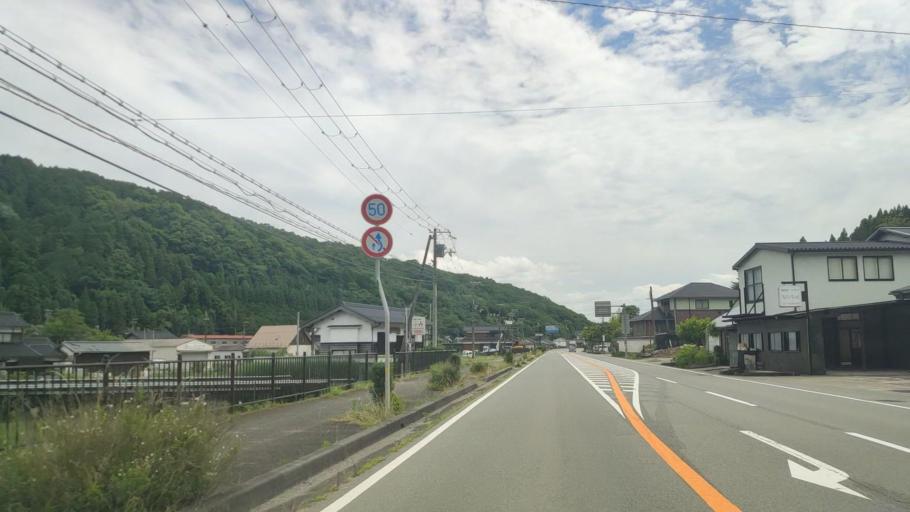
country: JP
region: Hyogo
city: Yamazakicho-nakabirose
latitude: 35.0467
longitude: 134.3696
